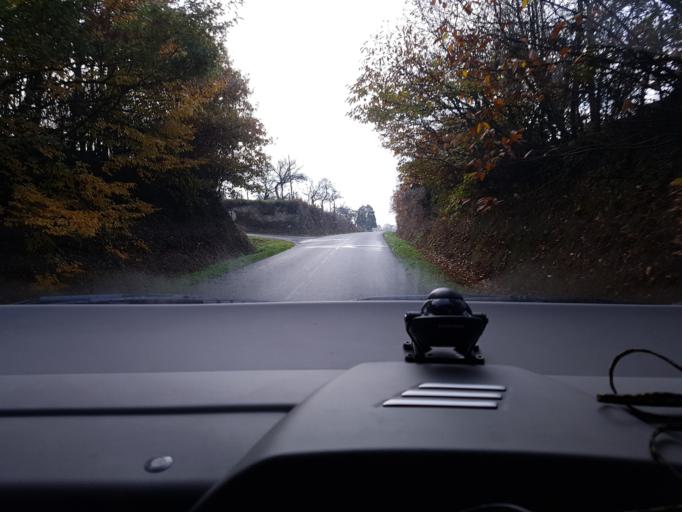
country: FR
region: Brittany
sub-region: Departement d'Ille-et-Vilaine
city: La Bouexiere
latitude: 48.1929
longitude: -1.4239
